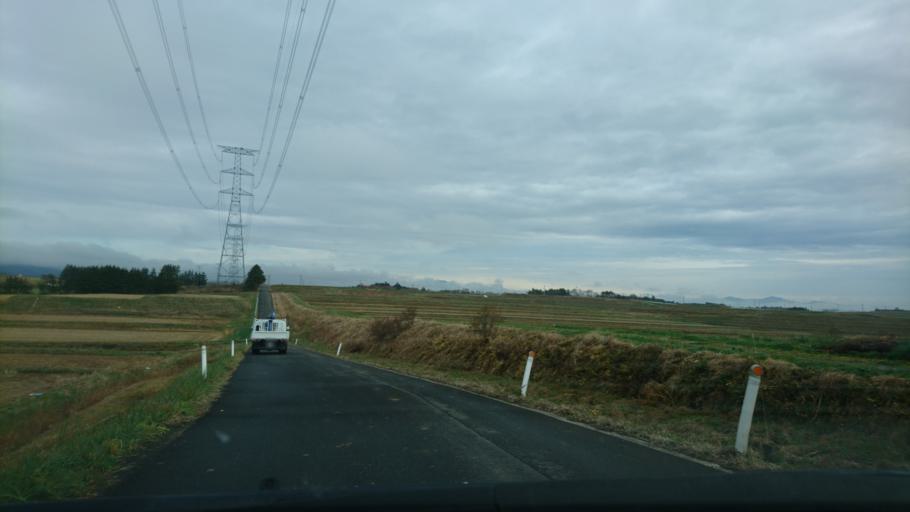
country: JP
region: Iwate
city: Ichinoseki
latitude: 38.8823
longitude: 141.1894
